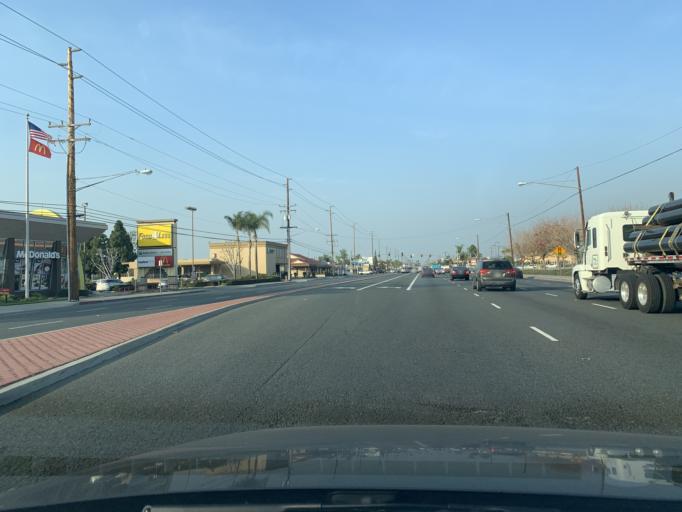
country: US
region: California
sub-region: Orange County
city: Stanton
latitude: 33.8009
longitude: -117.9930
